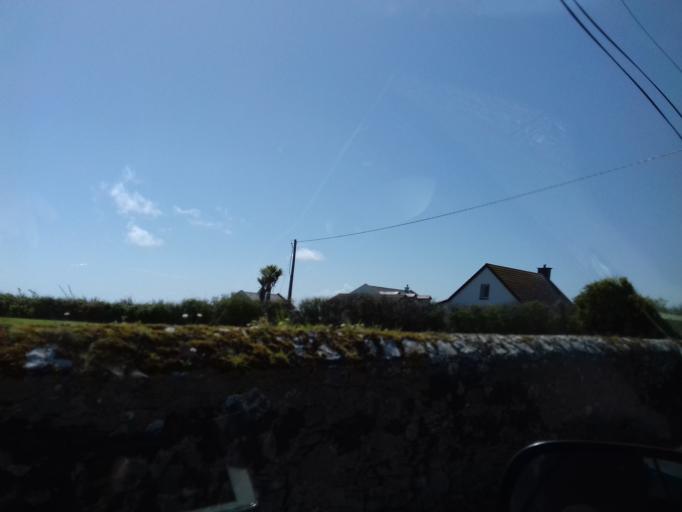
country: IE
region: Munster
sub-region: Waterford
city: Dunmore East
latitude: 52.1495
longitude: -6.9033
